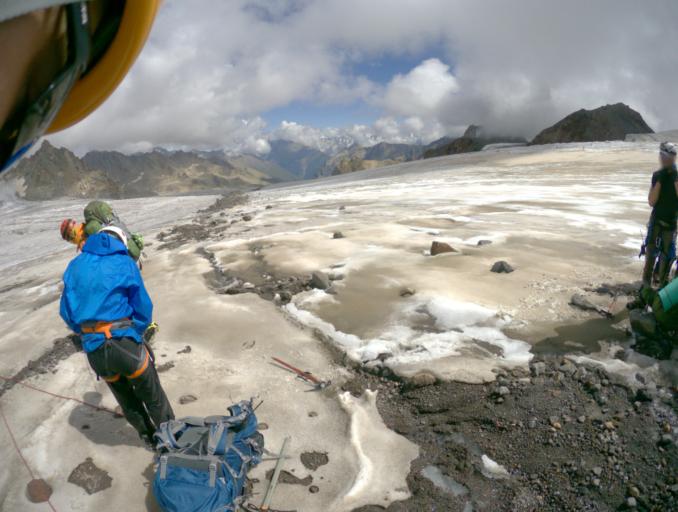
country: RU
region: Kabardino-Balkariya
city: Terskol
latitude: 43.3241
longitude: 42.5079
